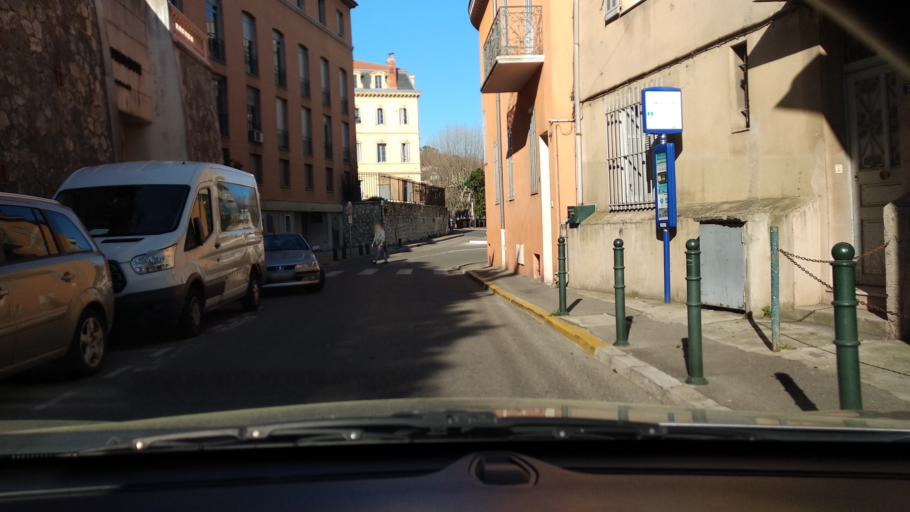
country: FR
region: Provence-Alpes-Cote d'Azur
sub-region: Departement des Alpes-Maritimes
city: Grasse
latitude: 43.6559
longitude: 6.9192
